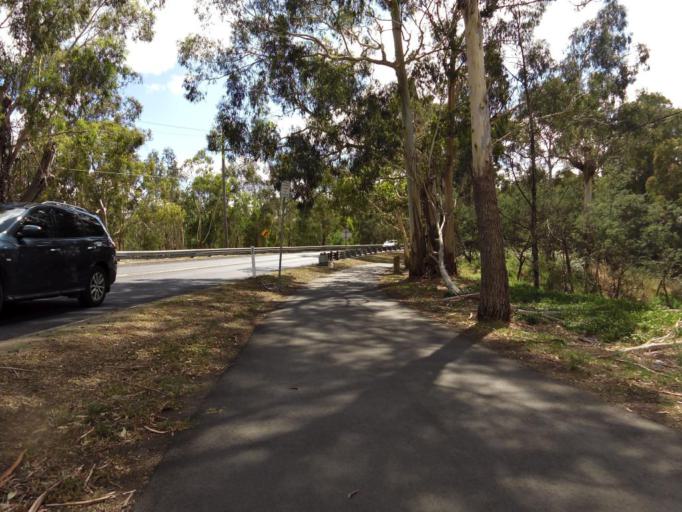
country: AU
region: Victoria
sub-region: Nillumbik
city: Eltham
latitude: -37.7313
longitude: 145.1419
